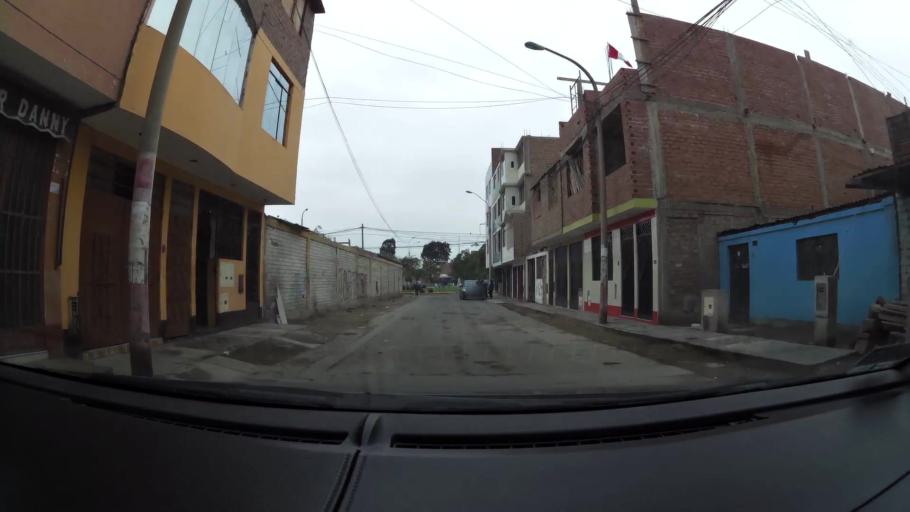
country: PE
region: Lima
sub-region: Lima
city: Independencia
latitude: -11.9701
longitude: -77.0771
